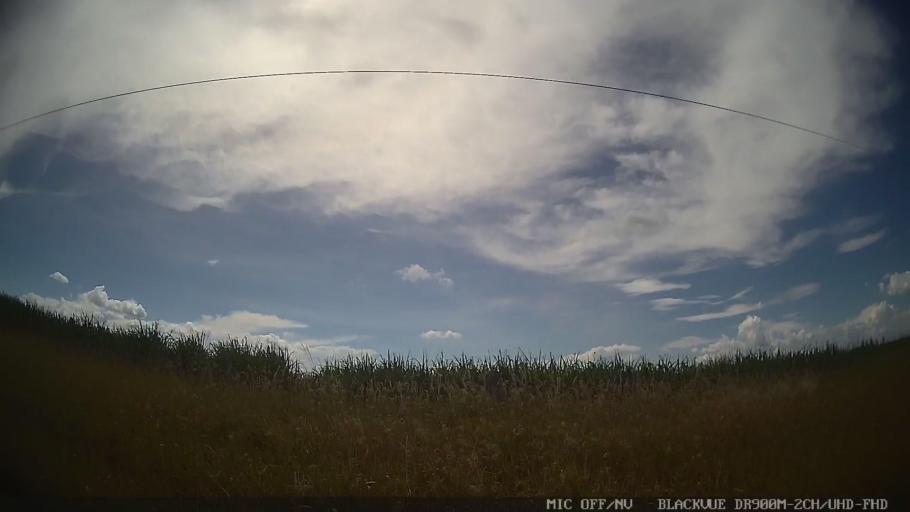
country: BR
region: Sao Paulo
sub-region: Conchas
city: Conchas
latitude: -22.9706
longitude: -47.9853
